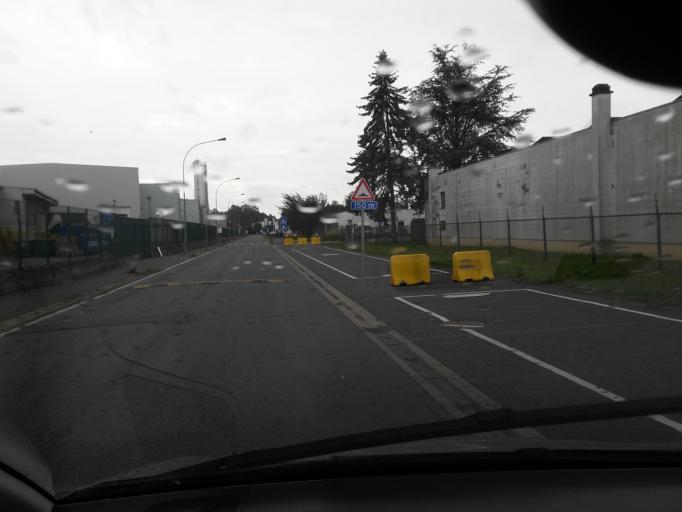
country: BE
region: Wallonia
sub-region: Province du Luxembourg
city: Arlon
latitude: 49.6763
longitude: 5.8175
